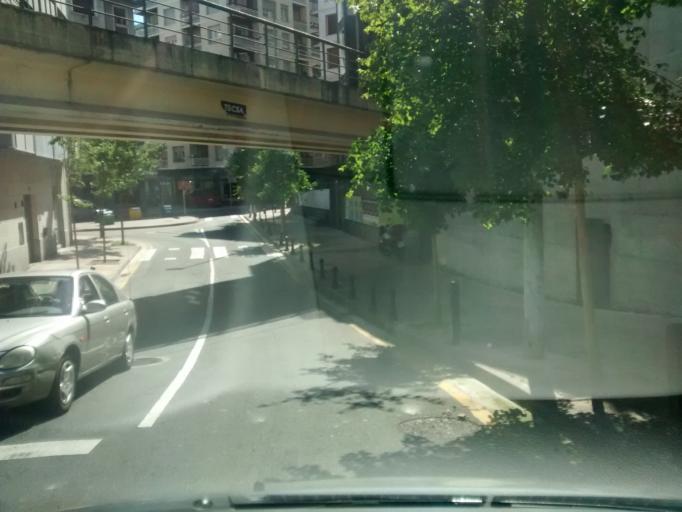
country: ES
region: Basque Country
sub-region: Provincia de Guipuzcoa
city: Eibar
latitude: 43.1859
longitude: -2.4722
